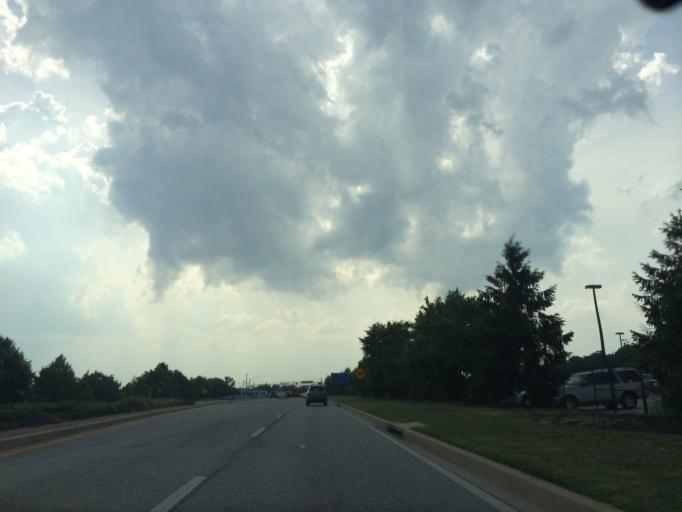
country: US
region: Maryland
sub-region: Anne Arundel County
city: Linthicum
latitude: 39.1904
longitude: -76.6730
